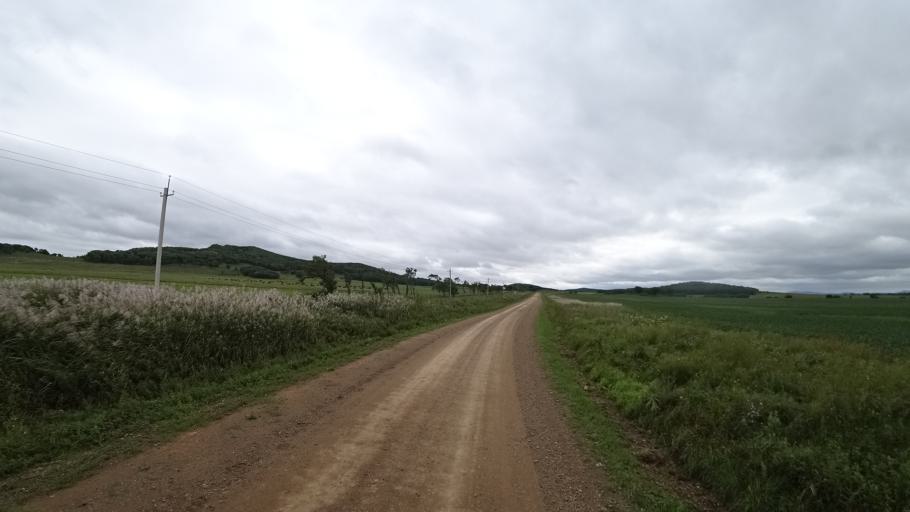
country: RU
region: Primorskiy
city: Chernigovka
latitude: 44.4778
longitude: 132.5787
